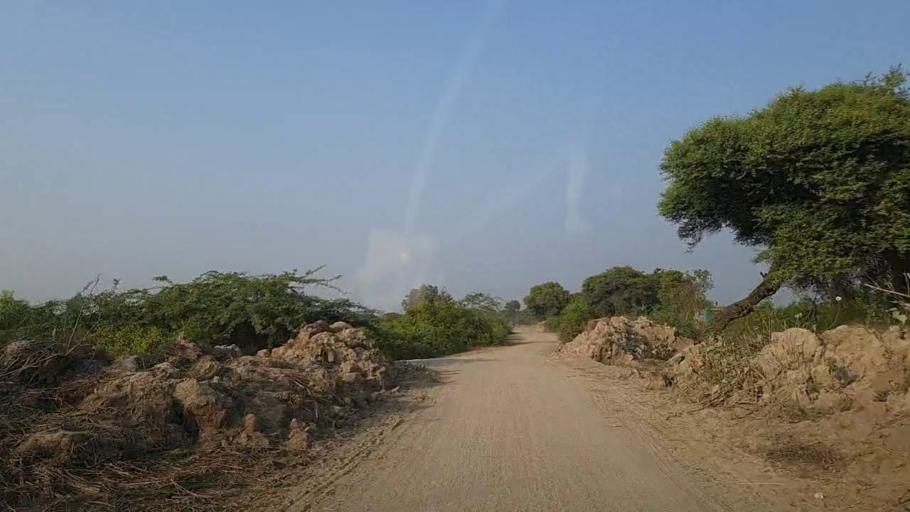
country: PK
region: Sindh
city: Thatta
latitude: 24.6914
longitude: 67.7923
